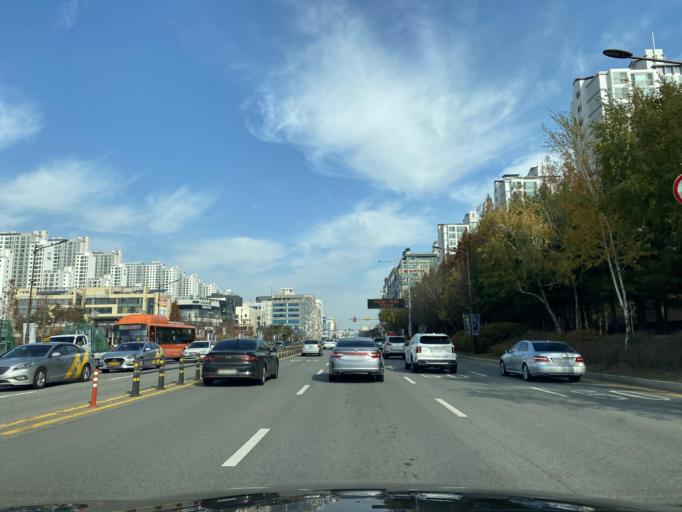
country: KR
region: Chungcheongnam-do
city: Cheonan
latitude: 36.8080
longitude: 127.1075
